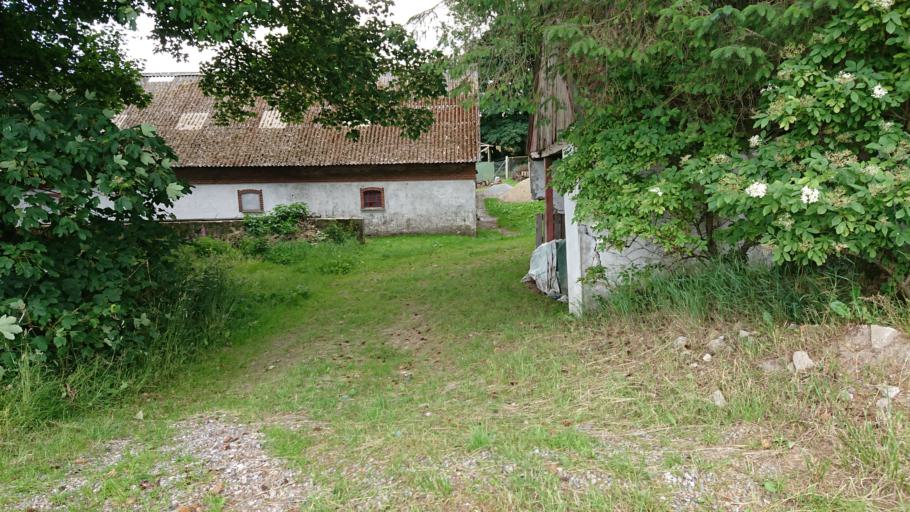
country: DK
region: North Denmark
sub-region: Jammerbugt Kommune
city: Brovst
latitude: 57.1294
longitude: 9.4101
